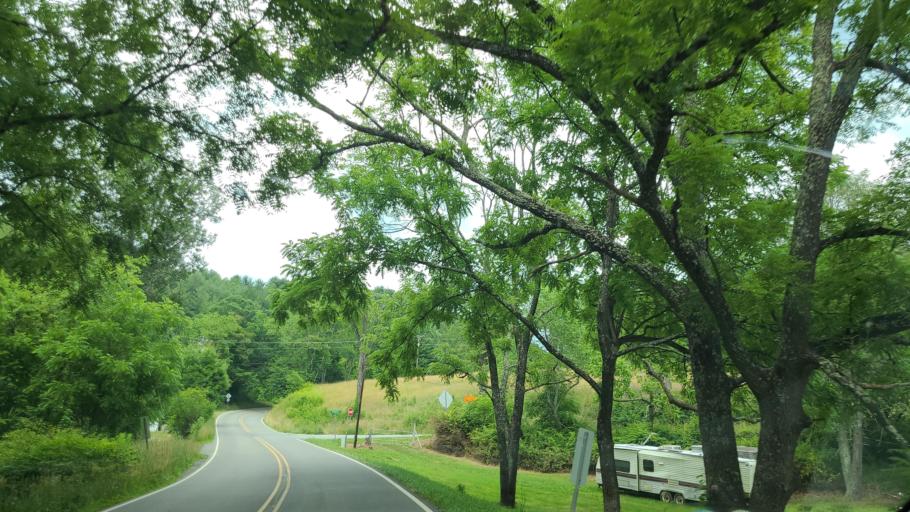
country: US
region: North Carolina
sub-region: Ashe County
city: Jefferson
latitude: 36.4016
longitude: -81.3872
